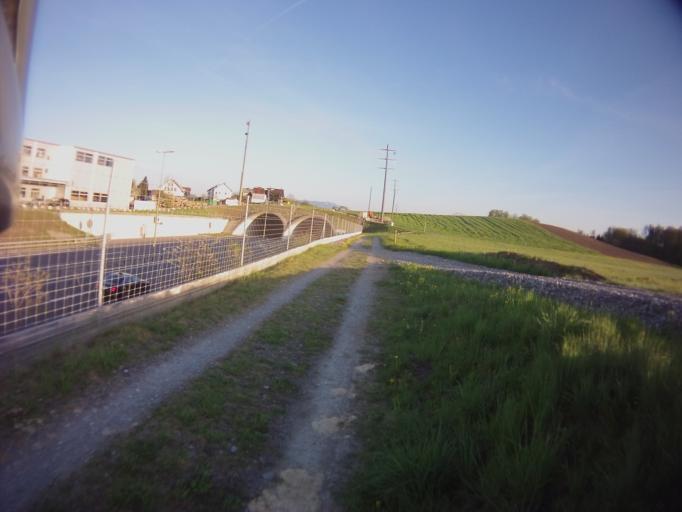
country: CH
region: Zurich
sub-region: Bezirk Affoltern
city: Mettmenstetten
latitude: 47.2449
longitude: 8.4534
